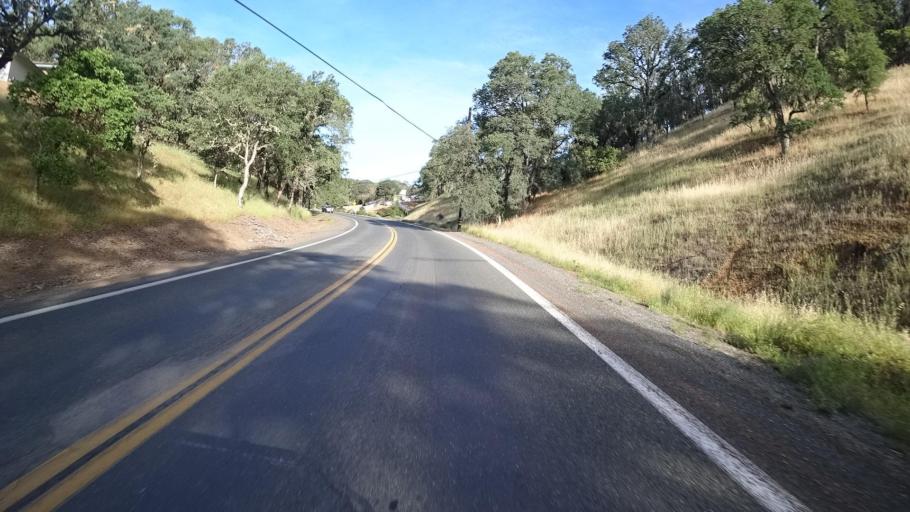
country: US
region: California
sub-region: Lake County
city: North Lakeport
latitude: 39.0799
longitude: -122.9179
